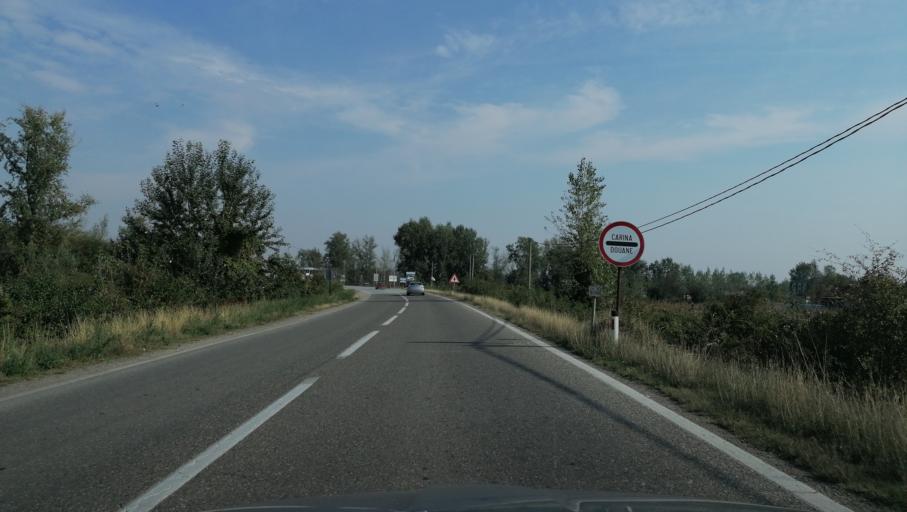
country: RS
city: Badovinci
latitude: 44.7755
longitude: 19.3319
